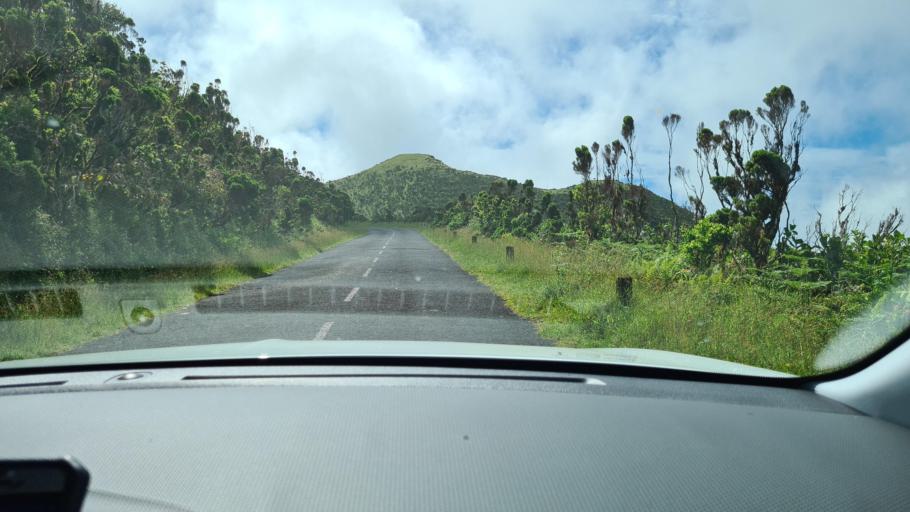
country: PT
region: Azores
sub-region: Sao Roque do Pico
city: Sao Roque do Pico
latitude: 38.6688
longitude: -28.1228
